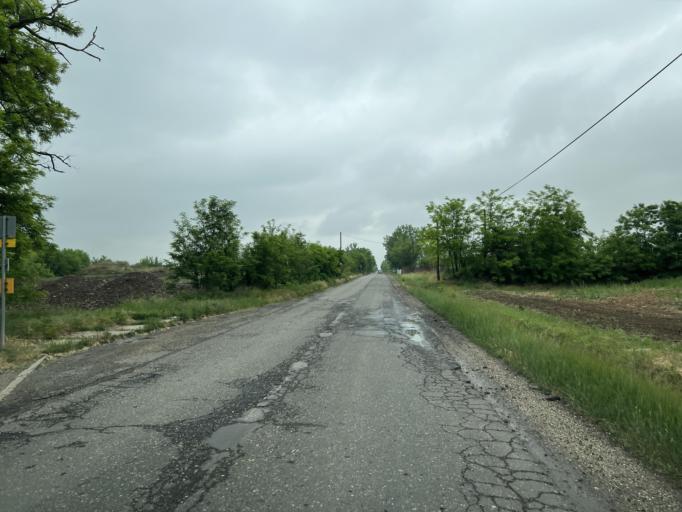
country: HU
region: Pest
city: Tura
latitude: 47.6189
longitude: 19.6119
